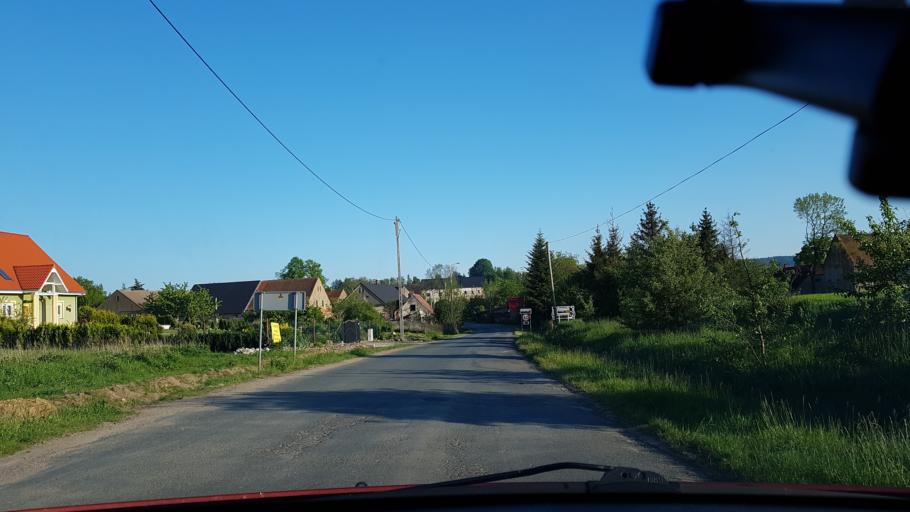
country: PL
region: Lower Silesian Voivodeship
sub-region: Powiat zabkowicki
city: Stoszowice
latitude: 50.6020
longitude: 16.7375
